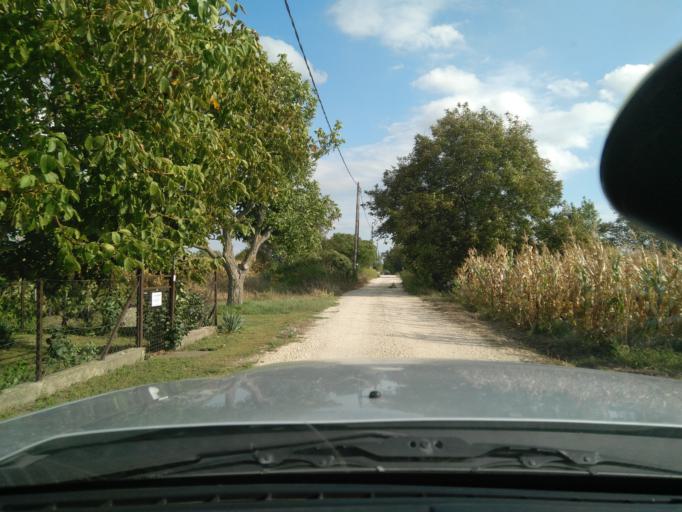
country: HU
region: Fejer
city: Bicske
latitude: 47.5037
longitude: 18.6584
